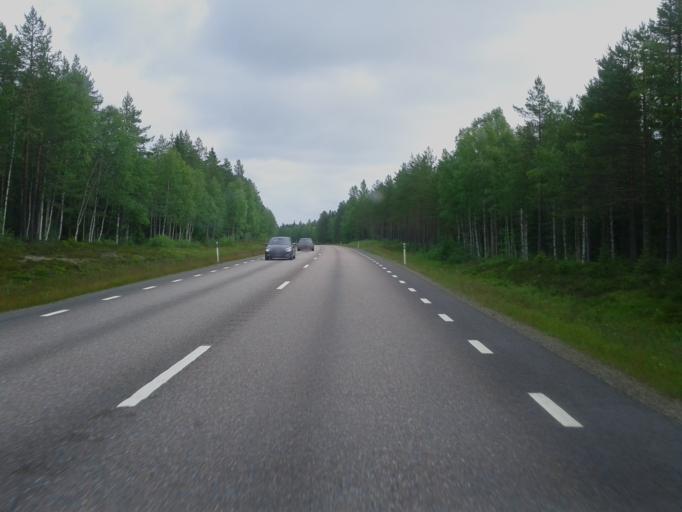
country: SE
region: Vaesterbotten
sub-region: Skelleftea Kommun
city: Burea
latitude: 64.3195
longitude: 21.1763
